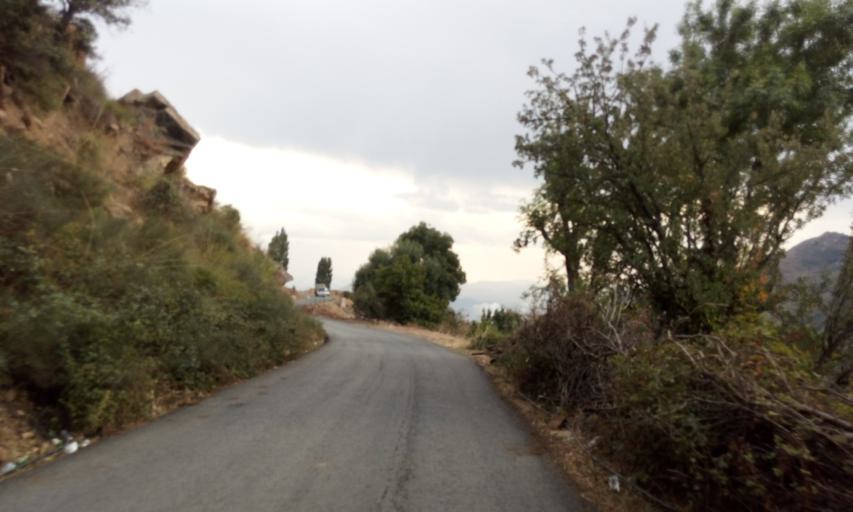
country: DZ
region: Tizi Ouzou
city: Chemini
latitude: 36.6061
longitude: 4.5702
